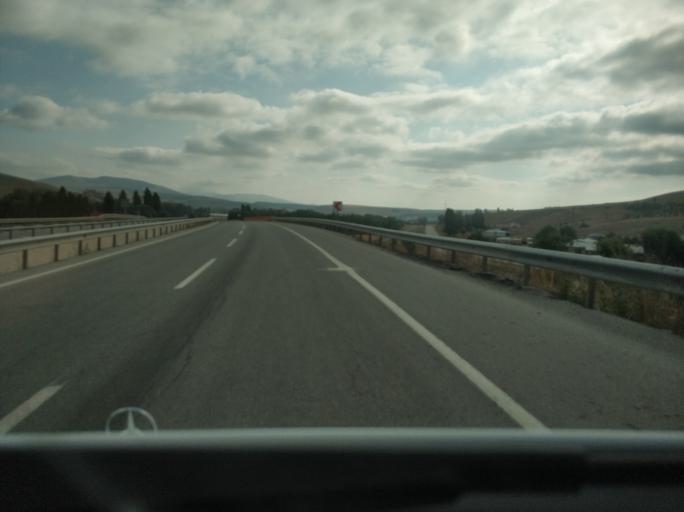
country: TR
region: Sivas
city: Yildizeli
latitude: 39.8646
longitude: 36.5764
